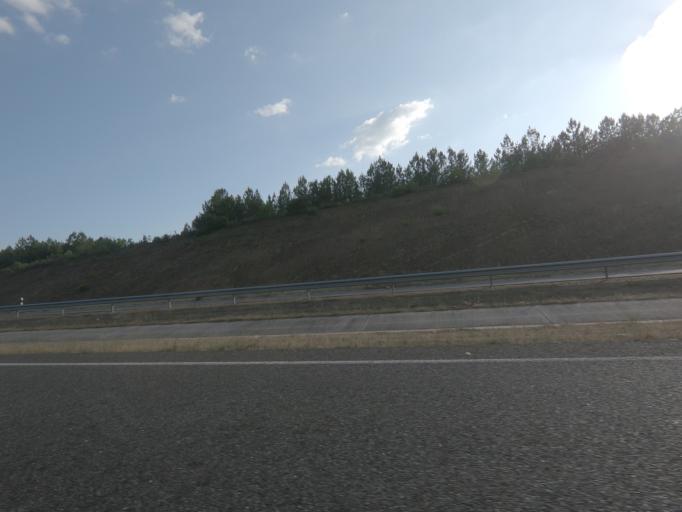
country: ES
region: Galicia
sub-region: Provincia de Ourense
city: Verin
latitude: 41.9003
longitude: -7.4255
